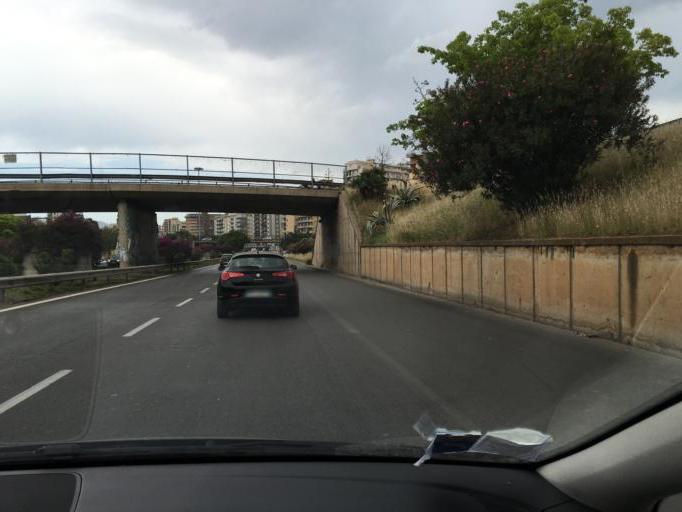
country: IT
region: Sicily
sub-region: Palermo
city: Palermo
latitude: 38.1387
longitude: 13.3311
